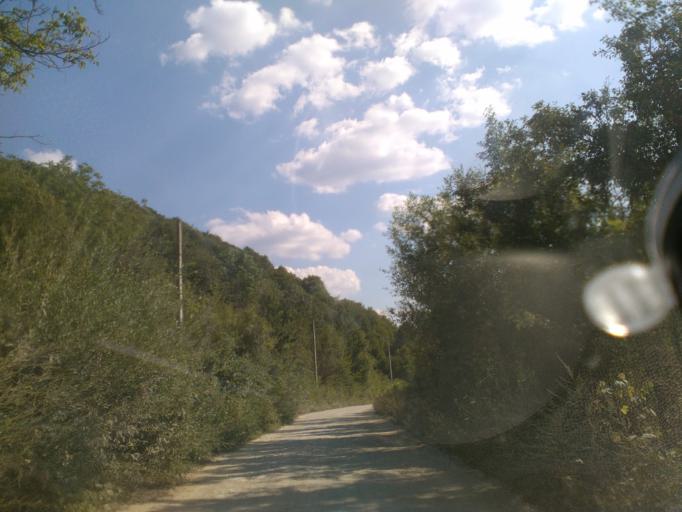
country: BA
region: Federation of Bosnia and Herzegovina
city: Orasac
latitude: 44.5142
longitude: 16.1278
